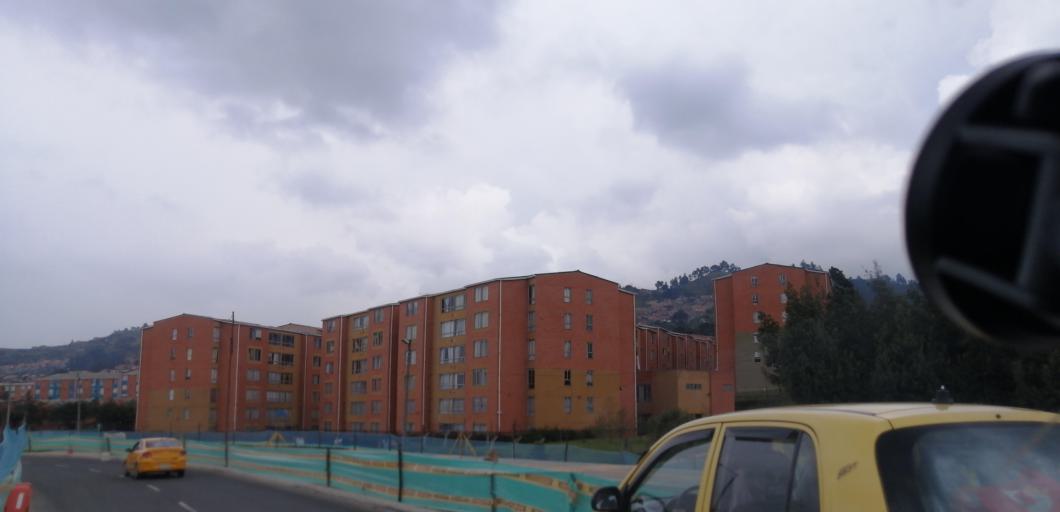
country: CO
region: Bogota D.C.
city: Bogota
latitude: 4.5277
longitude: -74.1194
